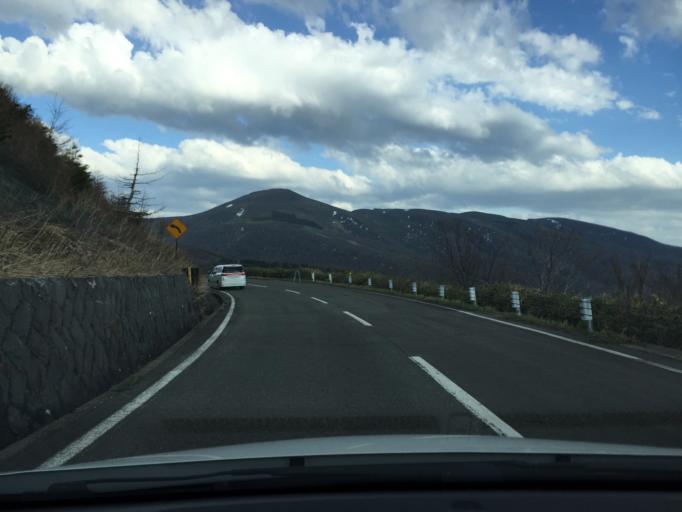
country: JP
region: Fukushima
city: Inawashiro
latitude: 37.6713
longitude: 140.2456
